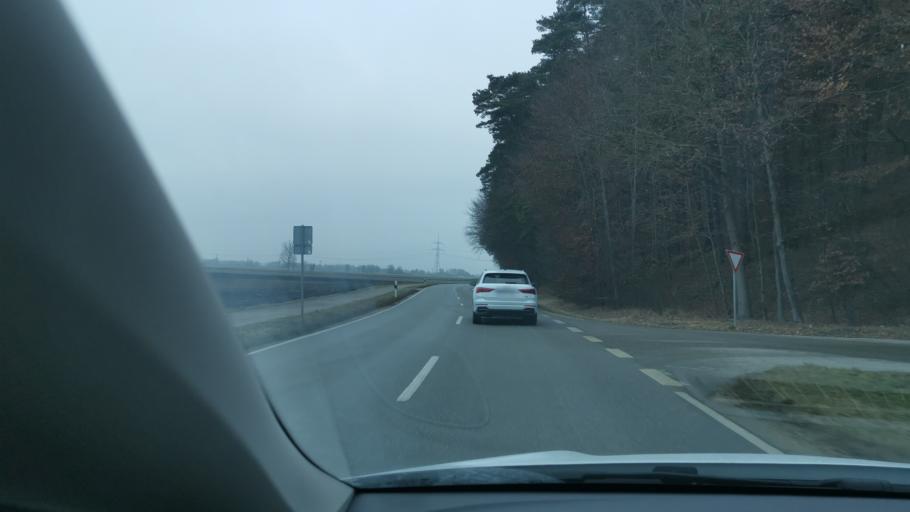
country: DE
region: Bavaria
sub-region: Swabia
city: Todtenweis
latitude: 48.5297
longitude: 10.9161
